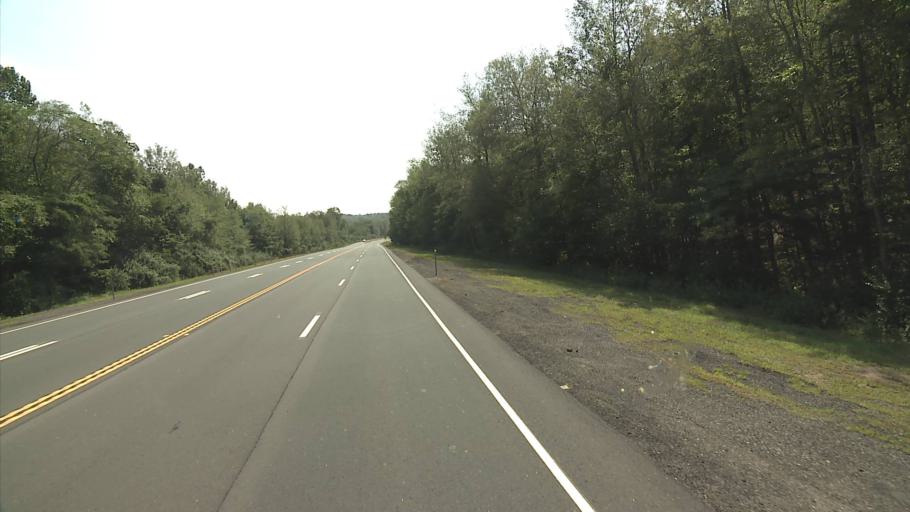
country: US
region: Connecticut
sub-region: Middlesex County
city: East Haddam
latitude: 41.4260
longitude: -72.4906
